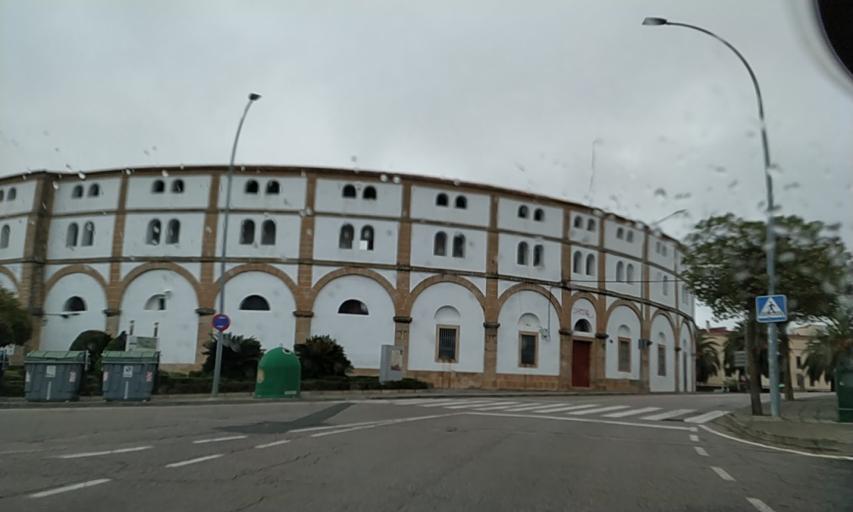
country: ES
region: Extremadura
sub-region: Provincia de Caceres
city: Caceres
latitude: 39.4802
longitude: -6.3764
